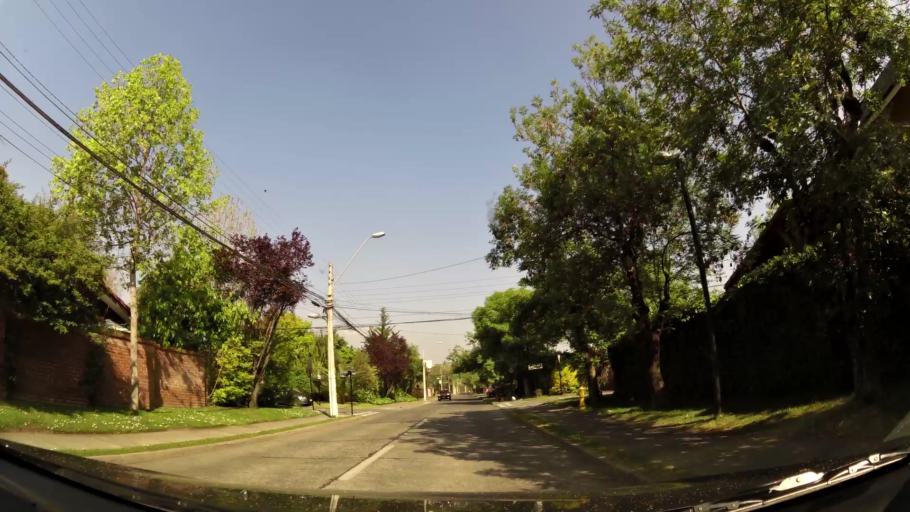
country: CL
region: Santiago Metropolitan
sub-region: Provincia de Santiago
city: Villa Presidente Frei, Nunoa, Santiago, Chile
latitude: -33.3814
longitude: -70.5554
